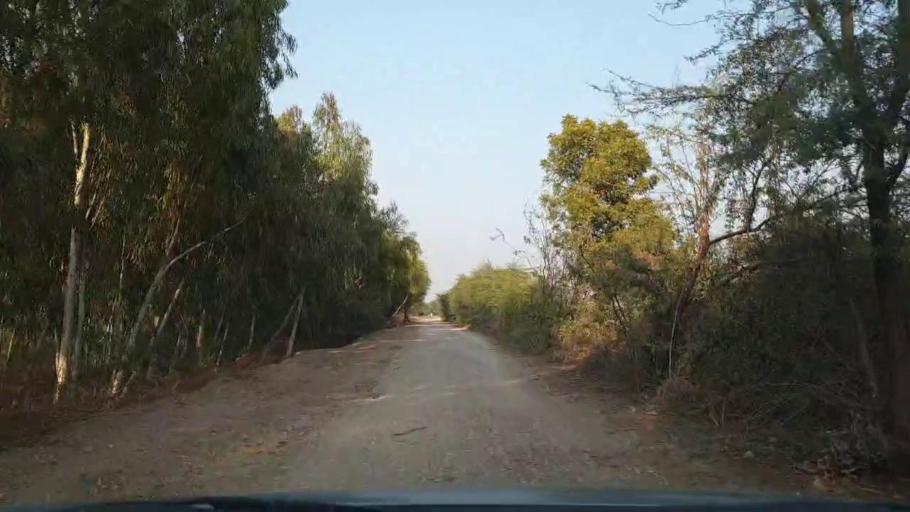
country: PK
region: Sindh
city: Tando Adam
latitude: 25.6933
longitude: 68.6347
